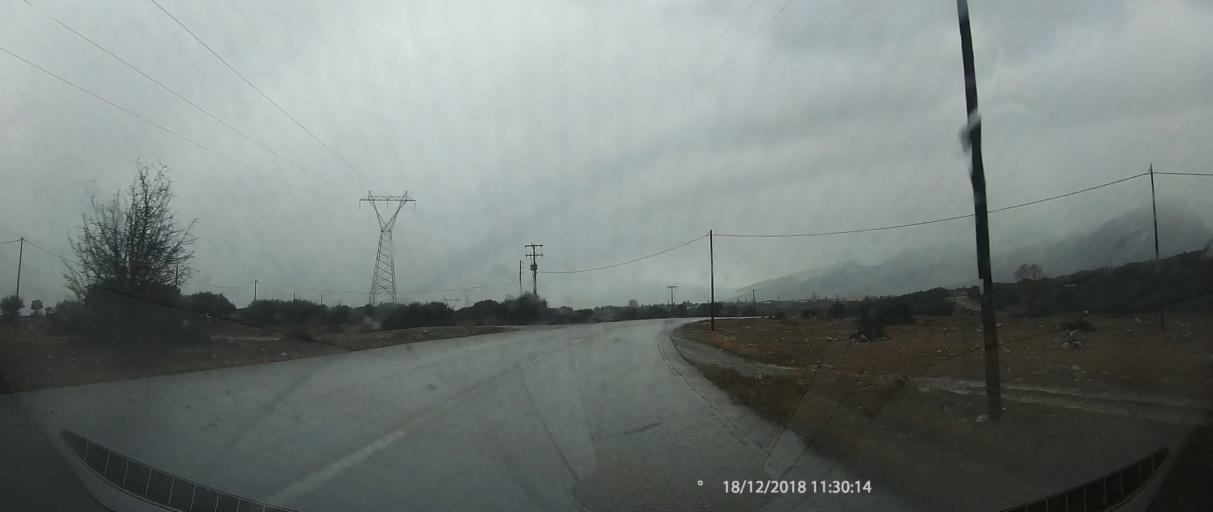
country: GR
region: Central Macedonia
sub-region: Nomos Pierias
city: Litochoro
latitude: 40.1257
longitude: 22.5228
